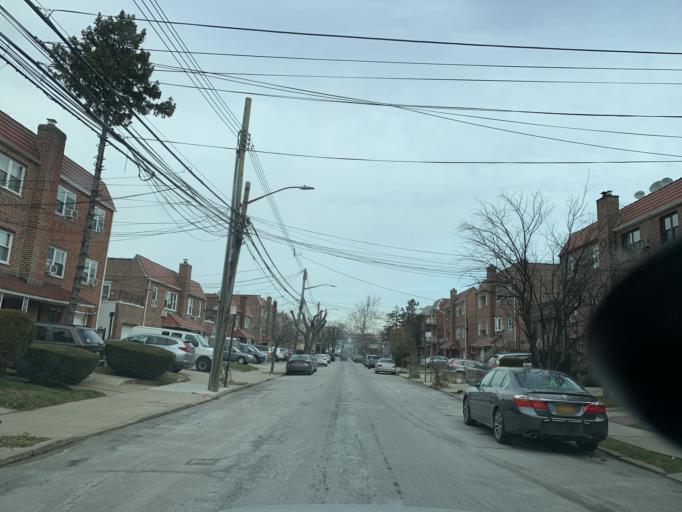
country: US
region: New York
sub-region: Queens County
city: Long Island City
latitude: 40.7353
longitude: -73.8840
